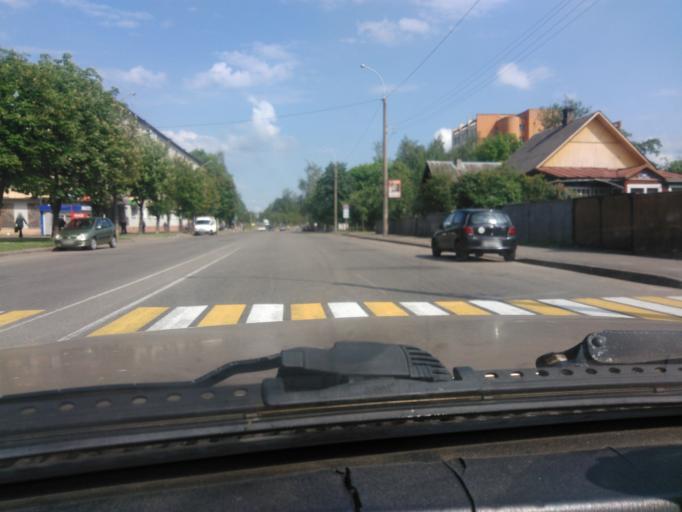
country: BY
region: Mogilev
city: Mahilyow
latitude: 53.9272
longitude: 30.3550
